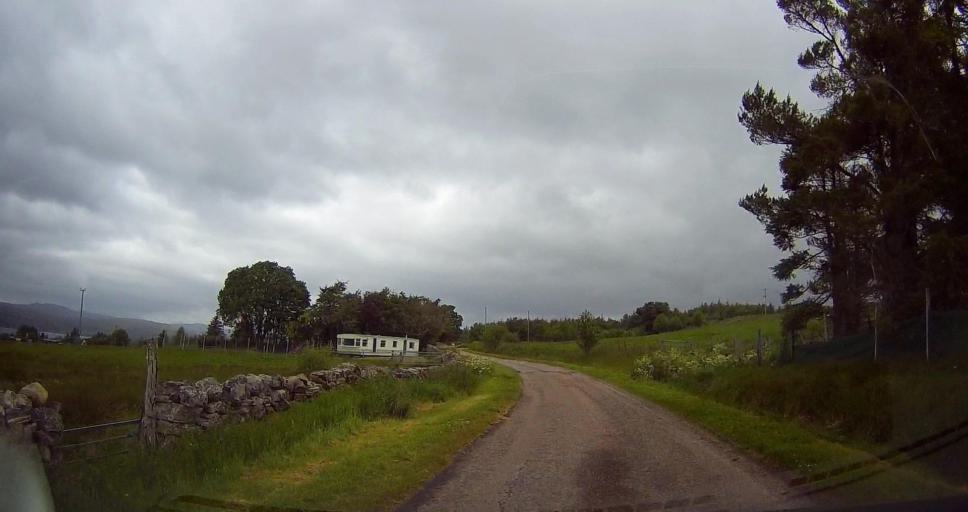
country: GB
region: Scotland
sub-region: Highland
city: Alness
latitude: 58.0798
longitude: -4.4474
